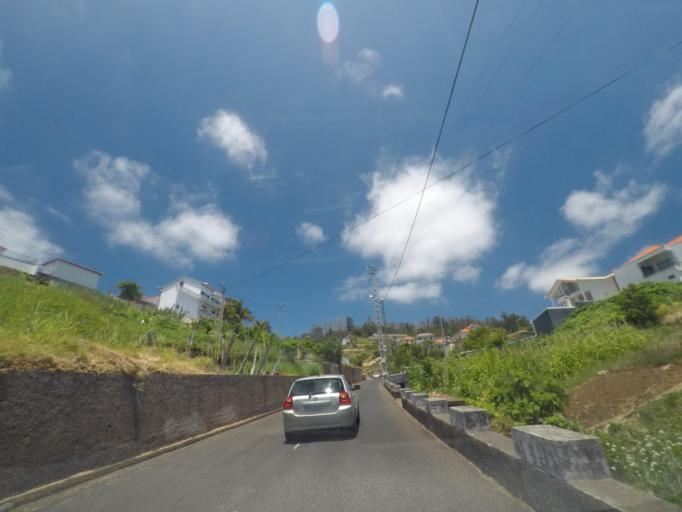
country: PT
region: Madeira
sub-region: Calheta
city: Estreito da Calheta
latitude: 32.7363
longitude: -17.1724
